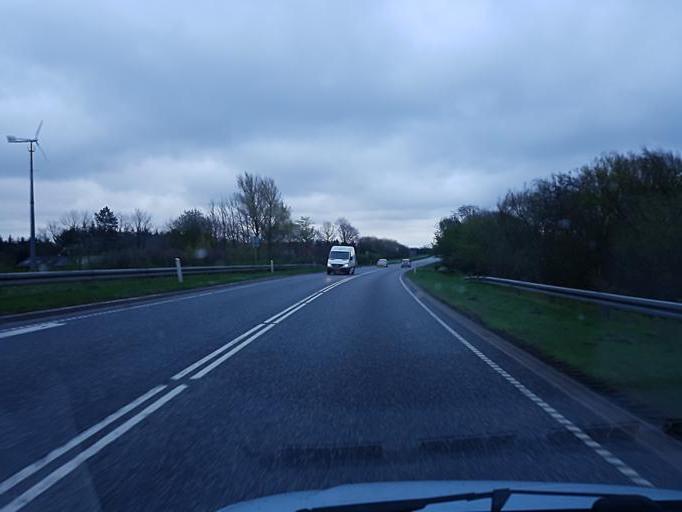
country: DK
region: South Denmark
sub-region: Esbjerg Kommune
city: Ribe
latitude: 55.3861
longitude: 8.7525
